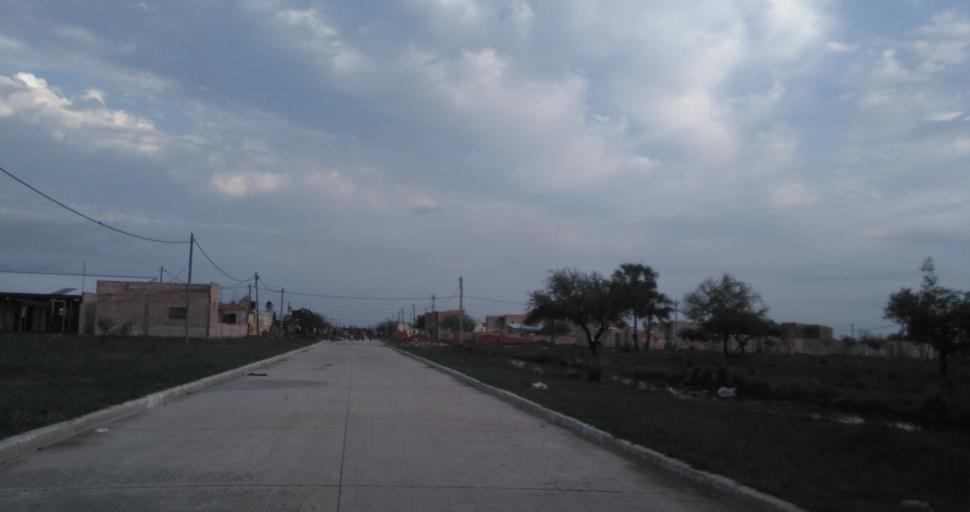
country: AR
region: Chaco
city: Resistencia
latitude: -27.4808
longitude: -59.0140
